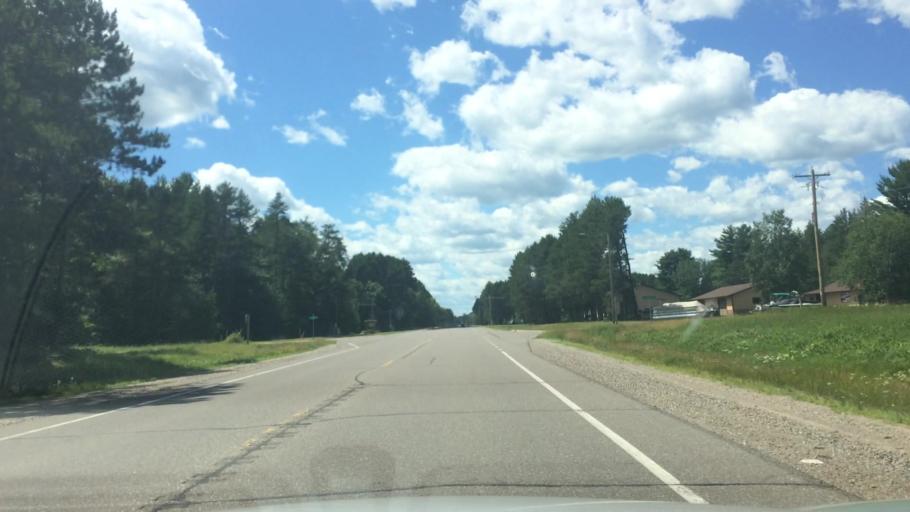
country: US
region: Wisconsin
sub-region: Vilas County
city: Lac du Flambeau
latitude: 45.8833
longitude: -89.7450
